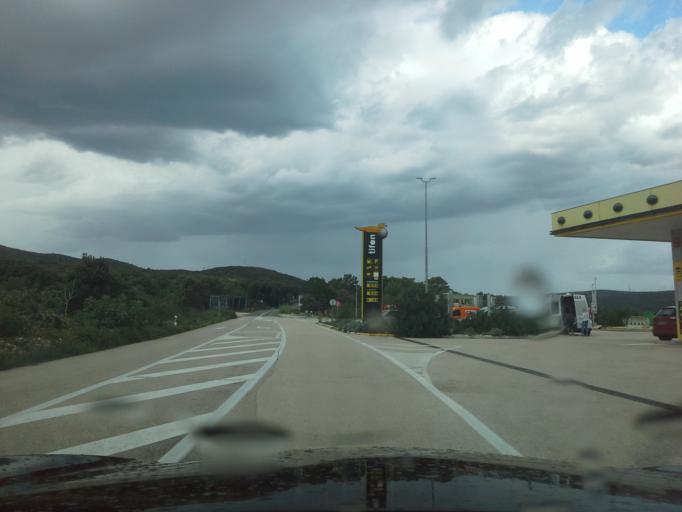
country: HR
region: Primorsko-Goranska
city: Mali Losinj
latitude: 44.6720
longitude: 14.3966
